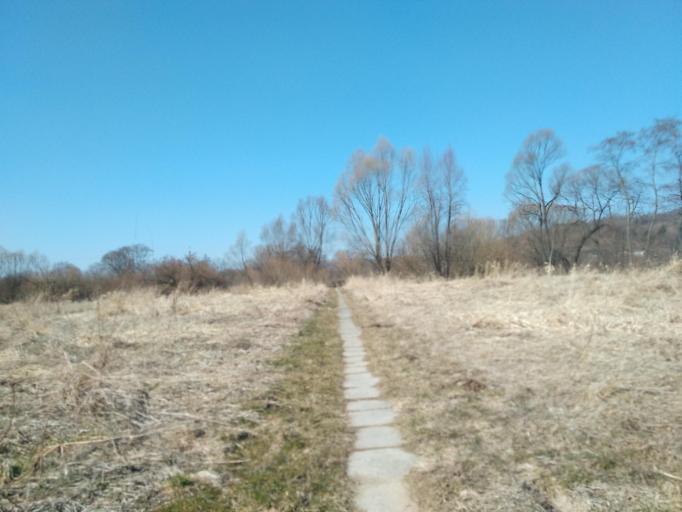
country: PL
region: Subcarpathian Voivodeship
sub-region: Powiat brzozowski
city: Domaradz
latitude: 49.7890
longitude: 21.9577
